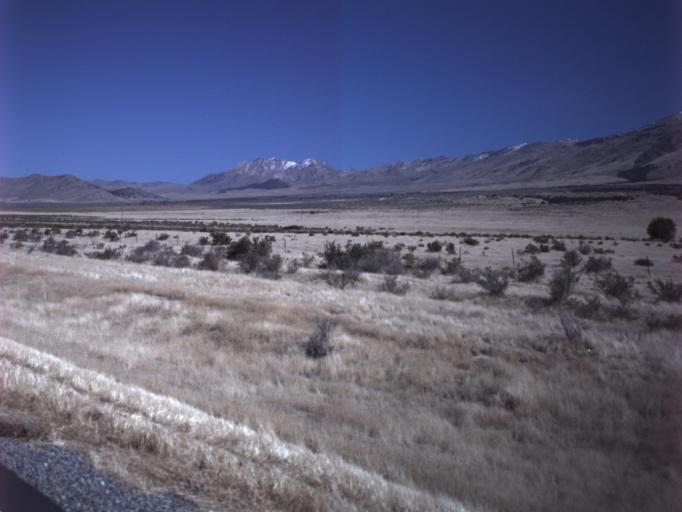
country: US
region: Utah
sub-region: Tooele County
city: Grantsville
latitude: 40.4676
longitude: -112.7467
